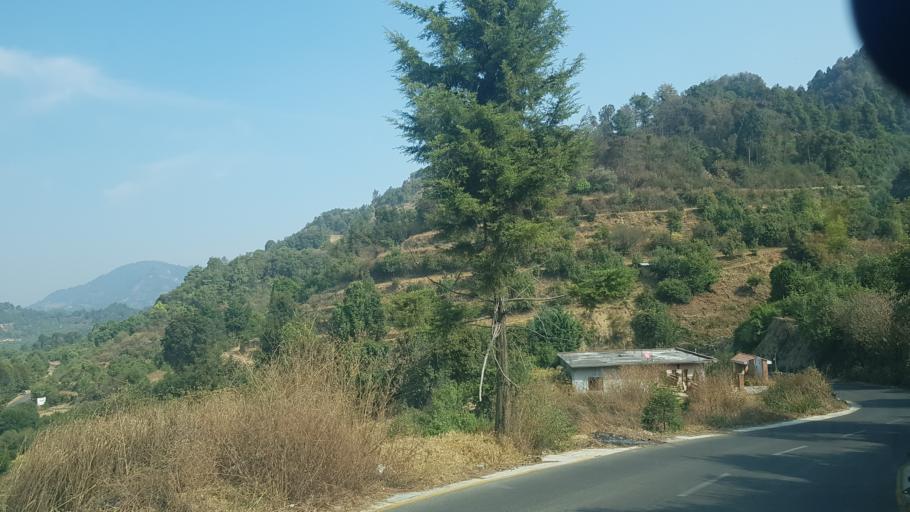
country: MX
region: Puebla
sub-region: Tochimilco
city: Santa Cruz Cuautomatitla
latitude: 18.8867
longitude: -98.6645
